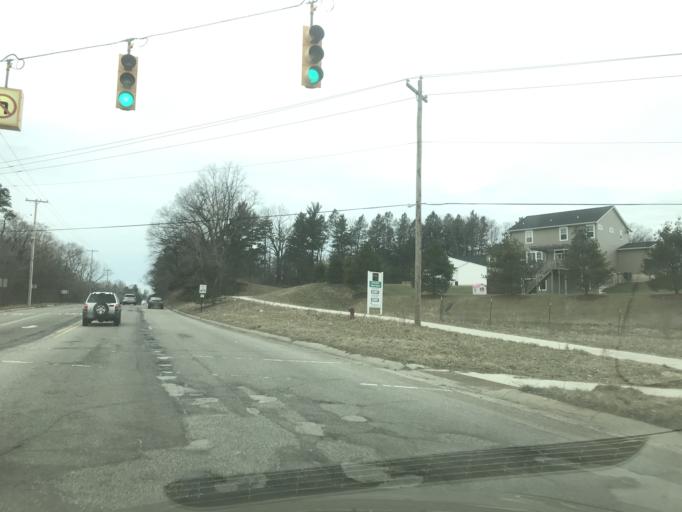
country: US
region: Michigan
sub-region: Ingham County
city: Okemos
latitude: 42.7553
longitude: -84.4425
